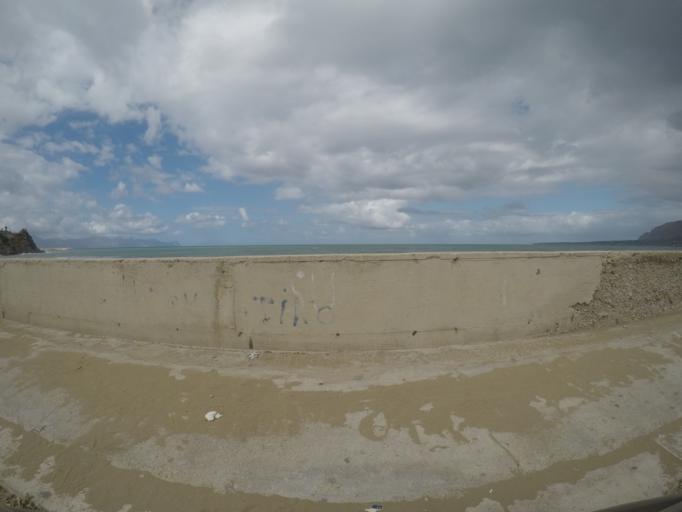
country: IT
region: Sicily
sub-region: Palermo
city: Trappeto
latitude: 38.0731
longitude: 13.0546
